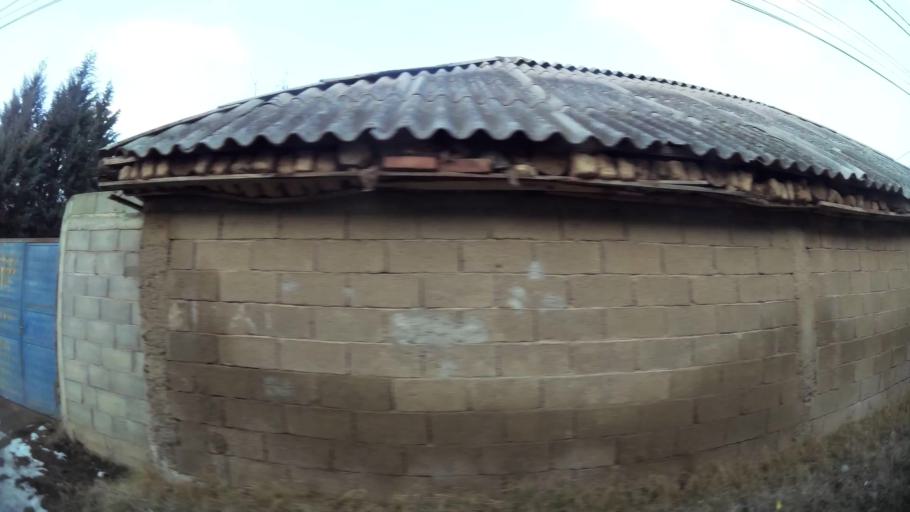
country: MK
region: Aracinovo
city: Arachinovo
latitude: 42.0221
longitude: 21.5605
